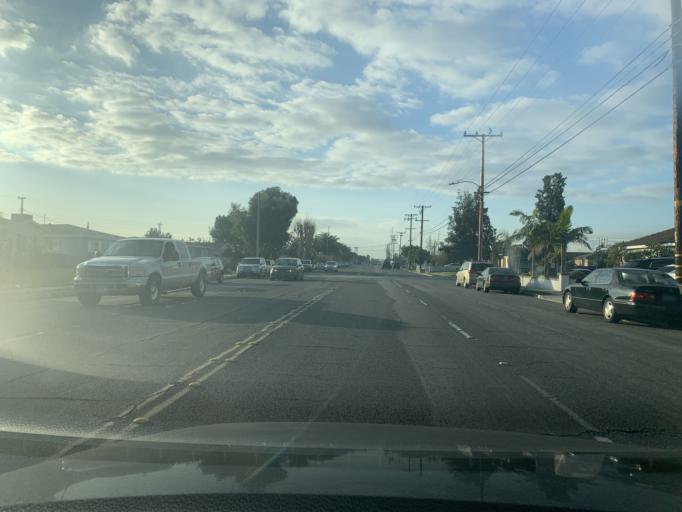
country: US
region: California
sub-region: Orange County
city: Westminster
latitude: 33.7719
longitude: -118.0162
